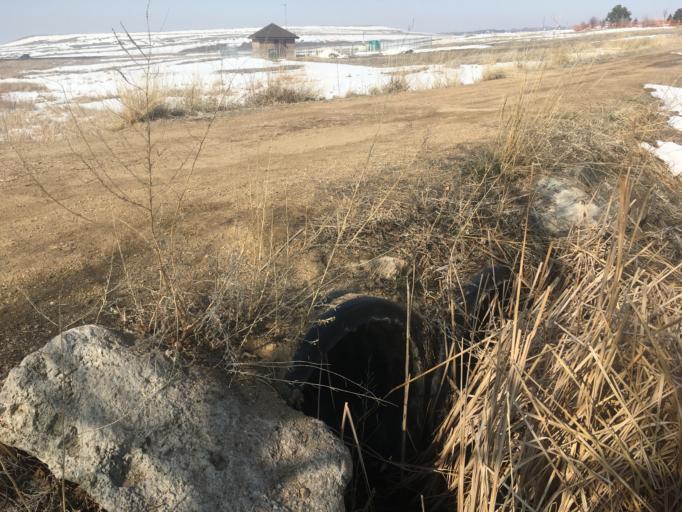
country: US
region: Colorado
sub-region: Boulder County
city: Lafayette
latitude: 39.9726
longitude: -105.0568
